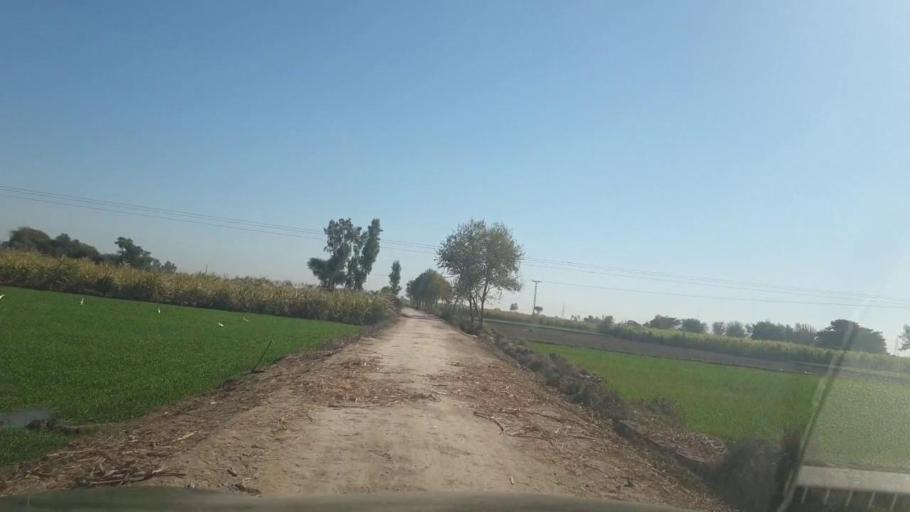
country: PK
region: Sindh
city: Ghotki
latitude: 27.9741
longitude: 69.3370
